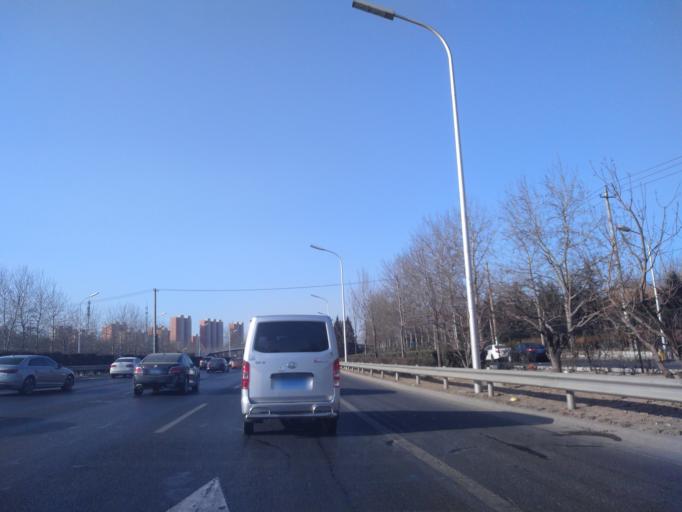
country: CN
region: Beijing
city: Jiugong
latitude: 39.8331
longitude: 116.4591
